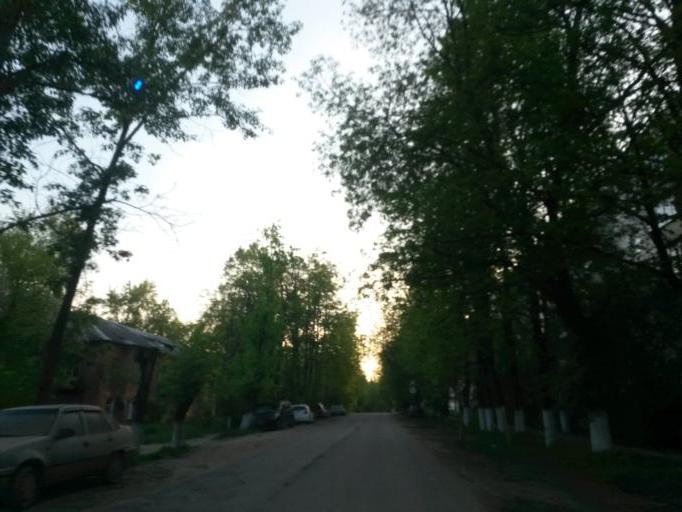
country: RU
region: Moskovskaya
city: Lyubuchany
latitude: 55.2412
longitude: 37.5418
